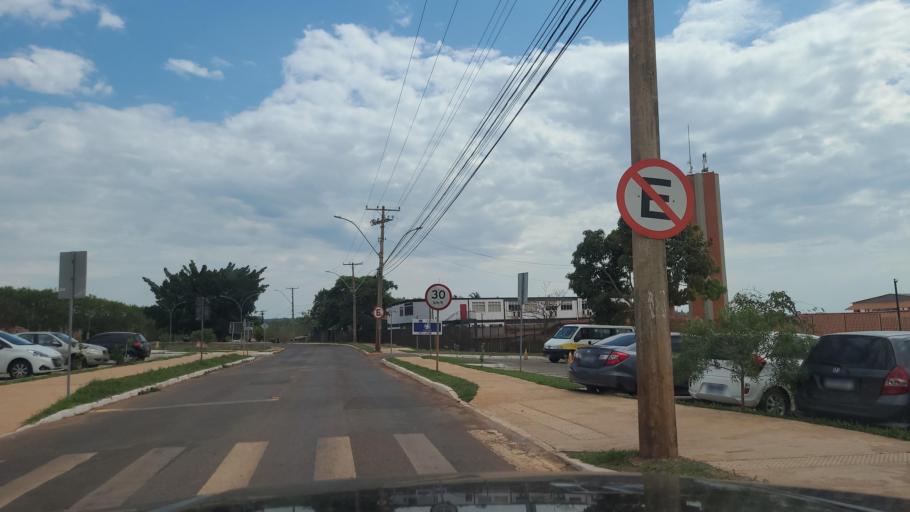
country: BR
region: Federal District
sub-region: Brasilia
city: Brasilia
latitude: -15.8536
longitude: -47.8501
